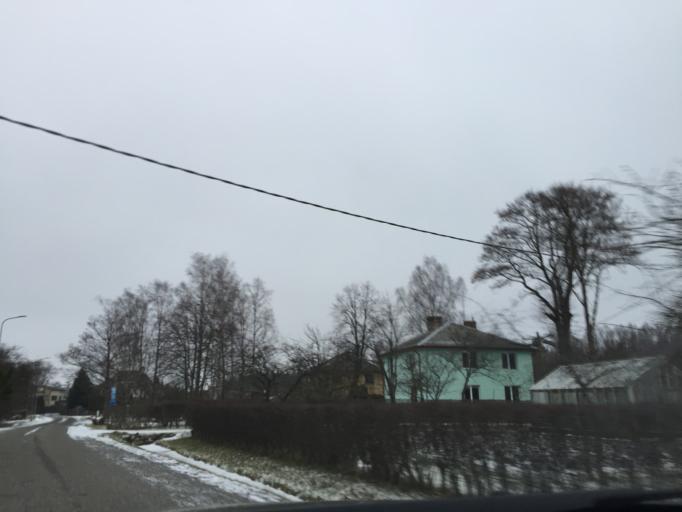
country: LV
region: Saulkrastu
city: Saulkrasti
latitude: 57.4955
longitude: 24.3856
